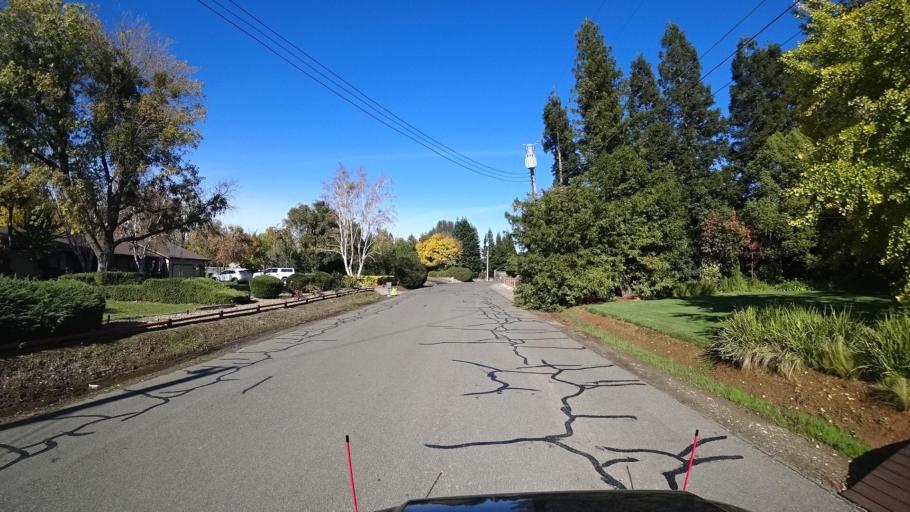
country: US
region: California
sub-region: Sacramento County
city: Vineyard
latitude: 38.4366
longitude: -121.3579
